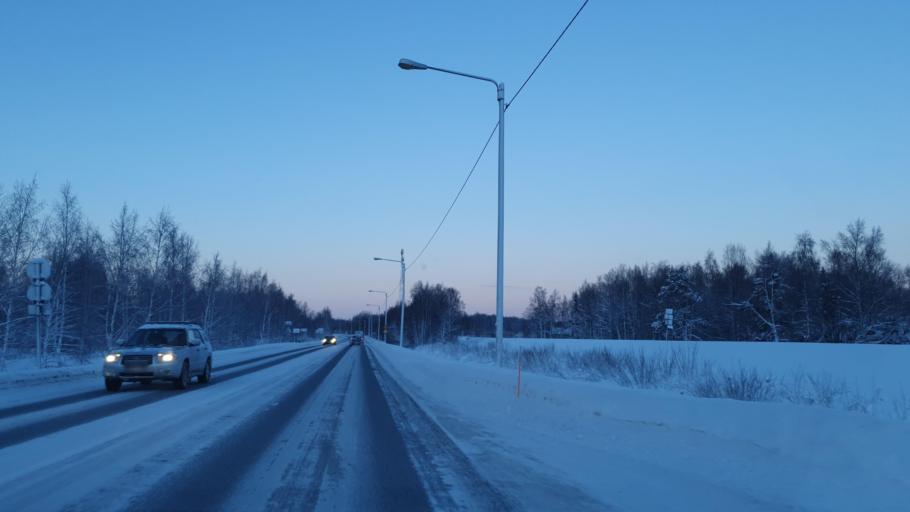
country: FI
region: Lapland
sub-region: Kemi-Tornio
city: Tornio
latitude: 65.8656
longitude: 24.1683
